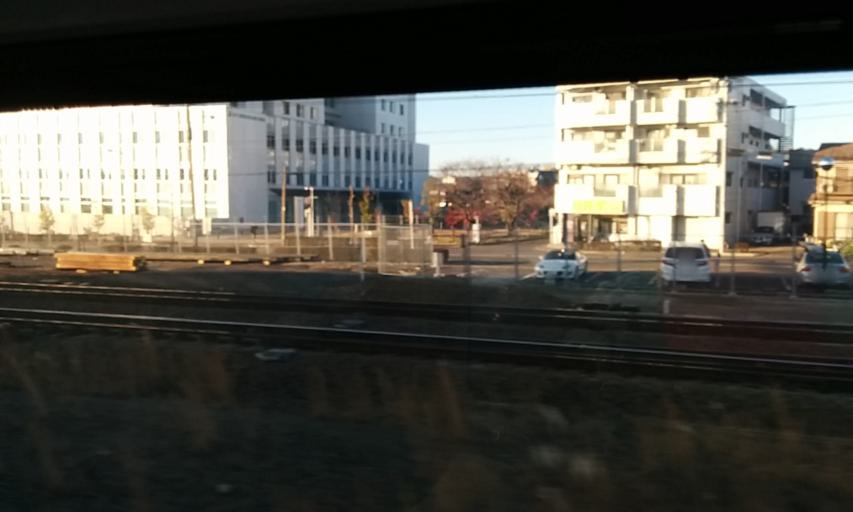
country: JP
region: Aichi
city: Seto
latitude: 35.2643
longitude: 137.0408
